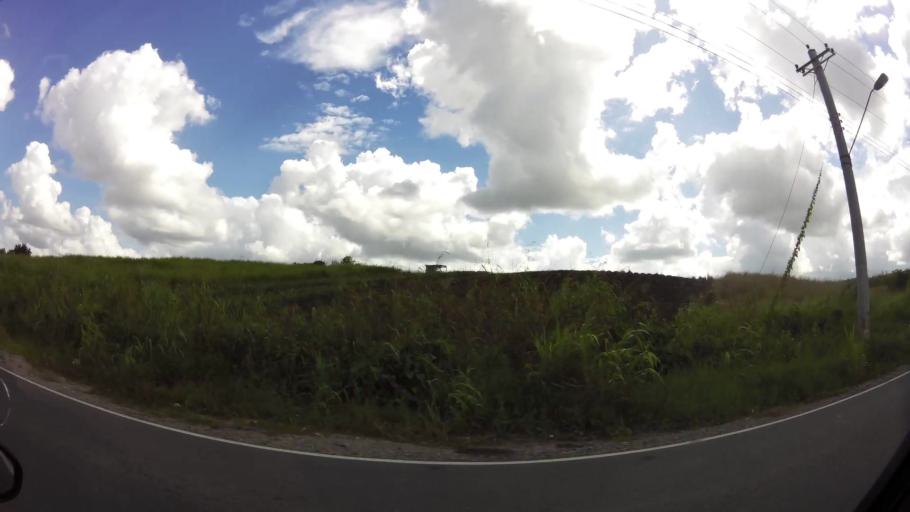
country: TT
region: Penal/Debe
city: Debe
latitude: 10.2313
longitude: -61.4827
